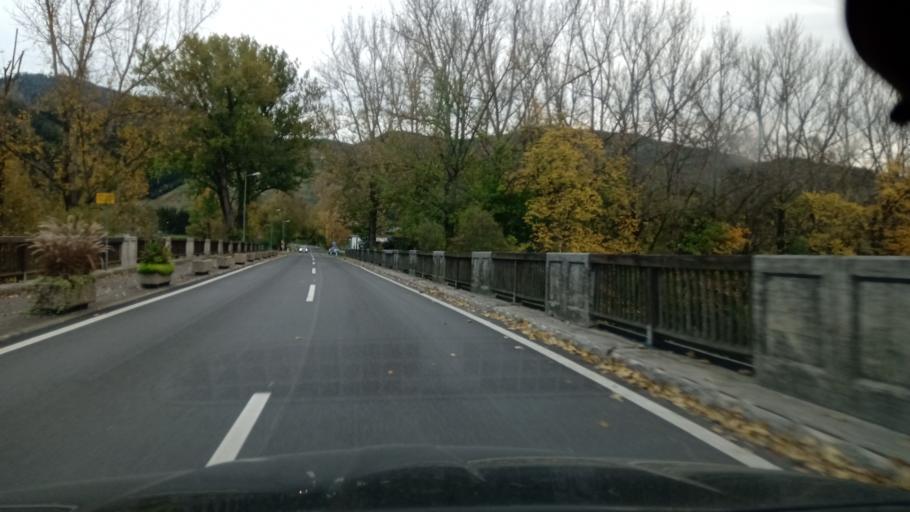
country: AT
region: Styria
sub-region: Politischer Bezirk Leoben
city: Niklasdorf
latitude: 47.3973
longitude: 15.1477
